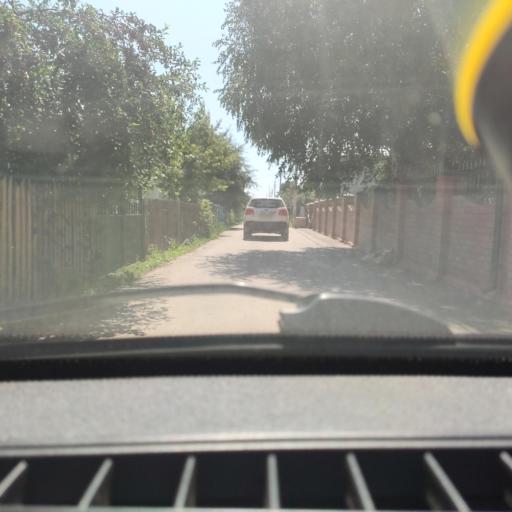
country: RU
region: Samara
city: Tol'yatti
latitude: 53.5960
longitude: 49.3057
